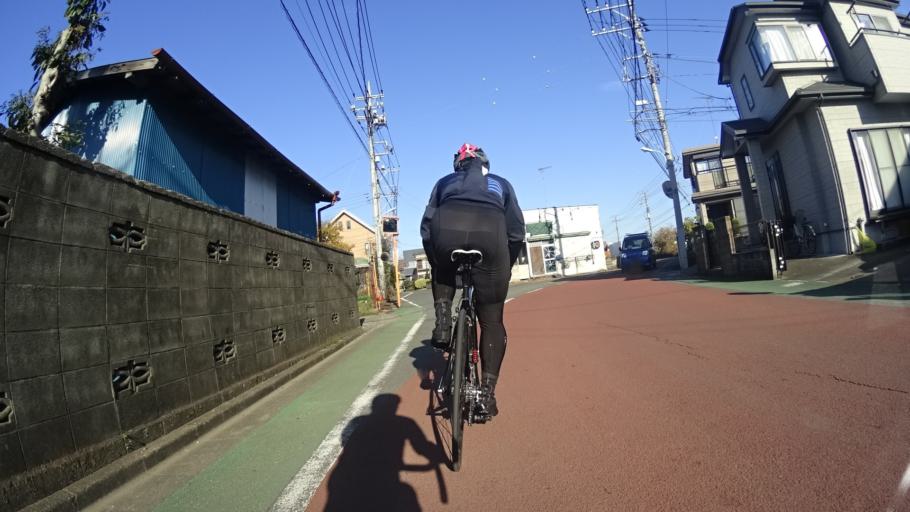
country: JP
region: Tokyo
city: Fussa
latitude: 35.7791
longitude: 139.3488
